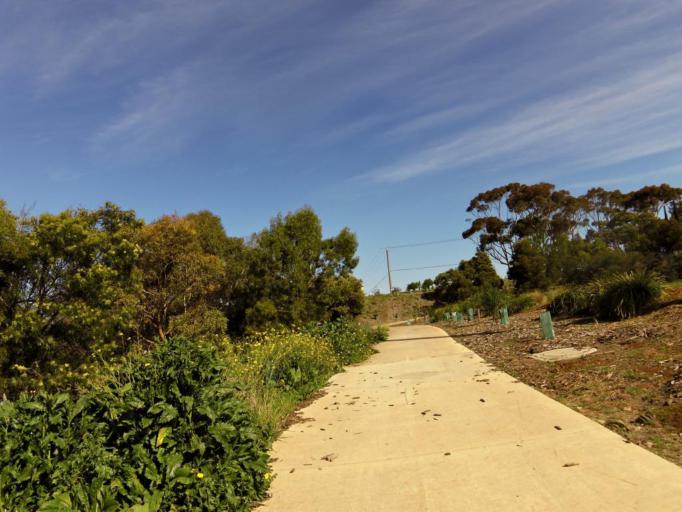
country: AU
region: Victoria
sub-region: Brimbank
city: Brooklyn
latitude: -37.8197
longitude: 144.8248
